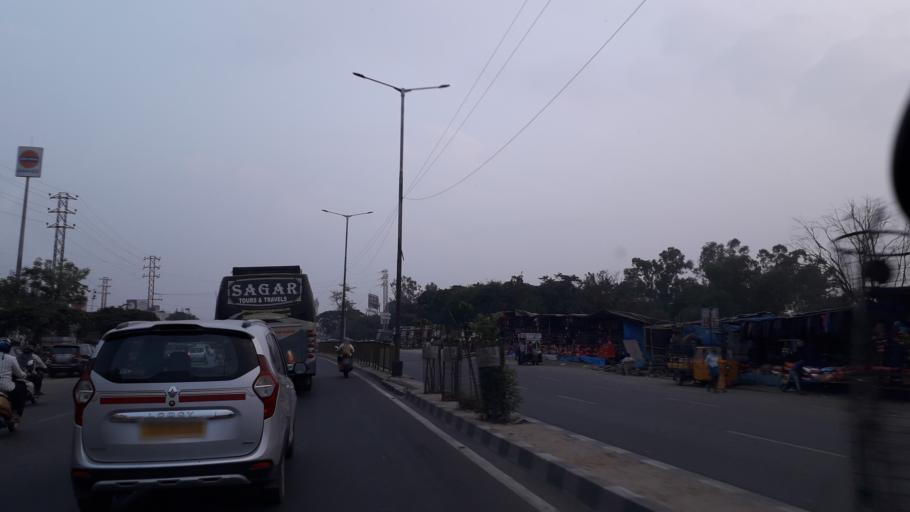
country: IN
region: Telangana
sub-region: Medak
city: Serilingampalle
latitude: 17.4976
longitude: 78.3144
